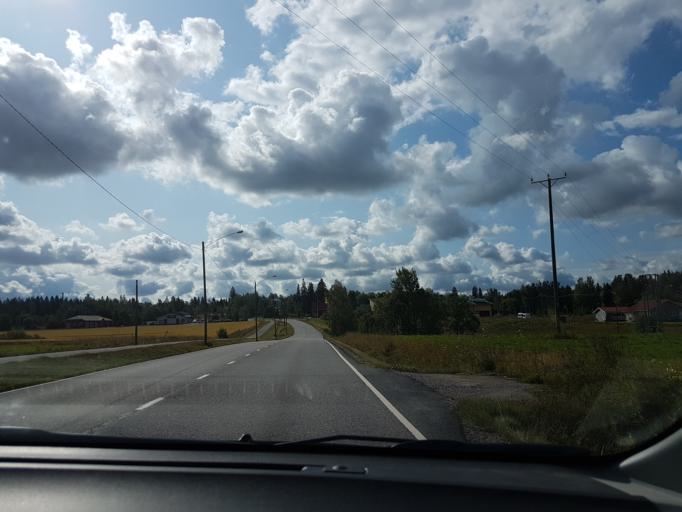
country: FI
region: Uusimaa
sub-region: Helsinki
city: Pornainen
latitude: 60.4829
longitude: 25.3697
